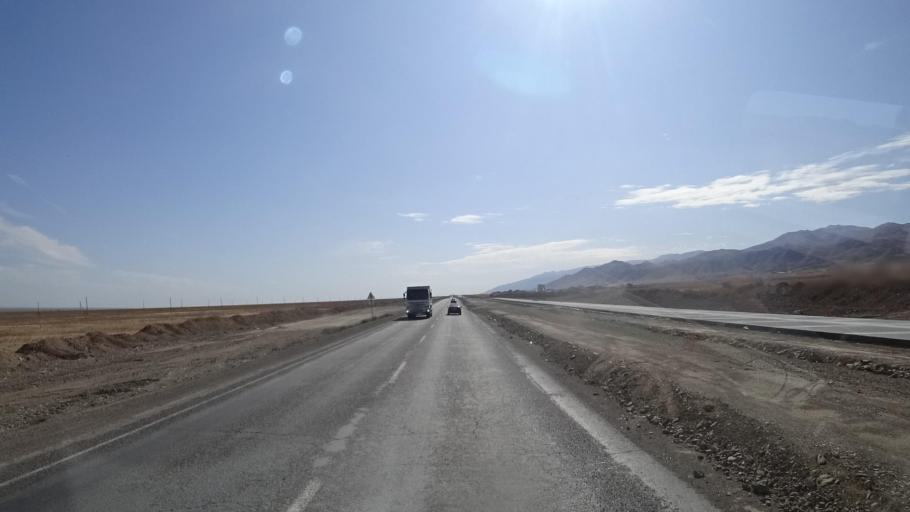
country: KG
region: Chuy
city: Ivanovka
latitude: 43.3955
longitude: 75.1275
